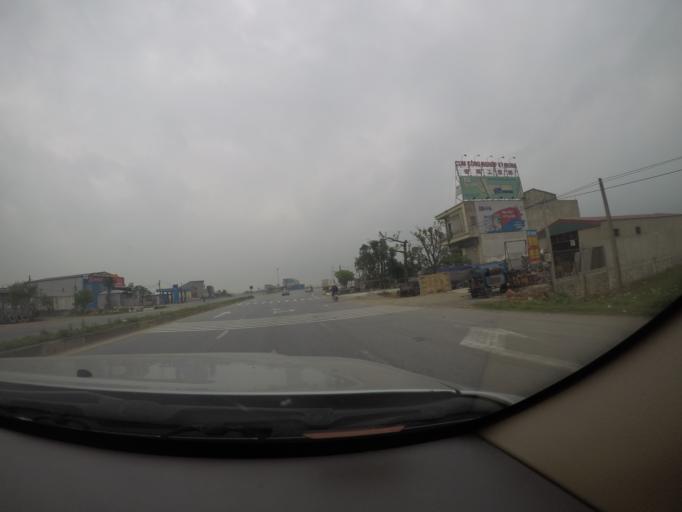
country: VN
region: Ha Tinh
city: Ky Anh
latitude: 18.1094
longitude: 106.2672
